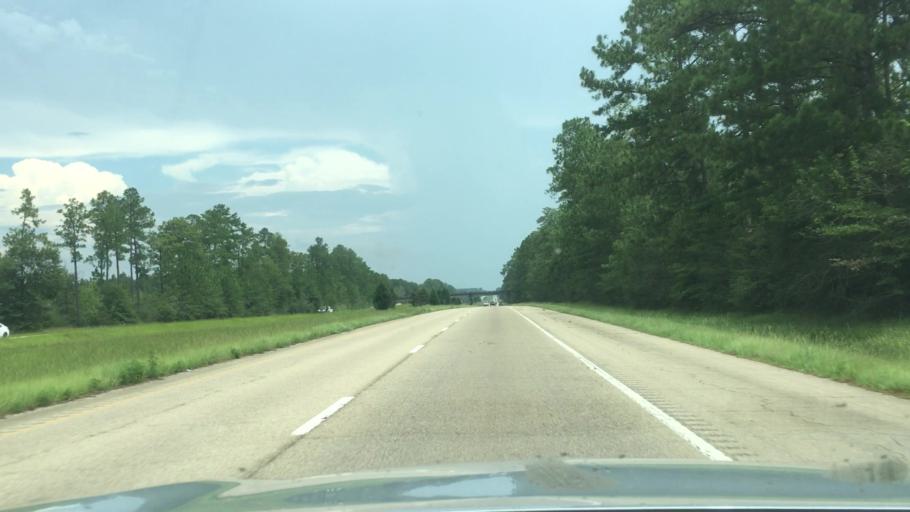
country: US
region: Mississippi
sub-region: Lamar County
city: Lumberton
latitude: 30.9749
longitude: -89.4317
